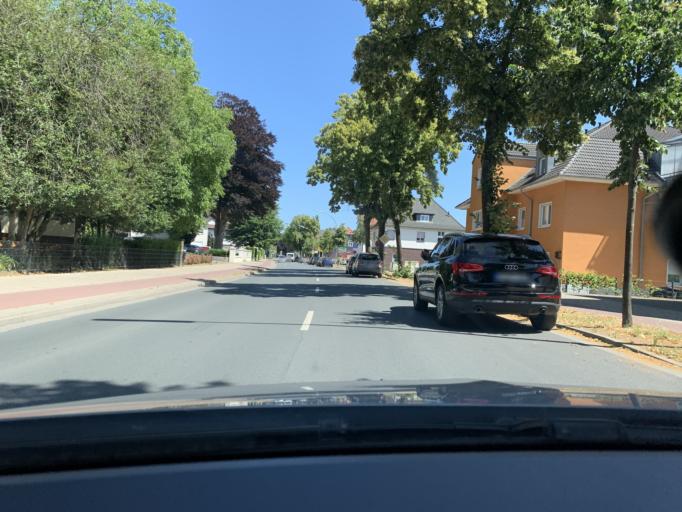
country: DE
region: North Rhine-Westphalia
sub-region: Regierungsbezirk Detmold
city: Rheda-Wiedenbruck
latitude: 51.8554
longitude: 8.2900
